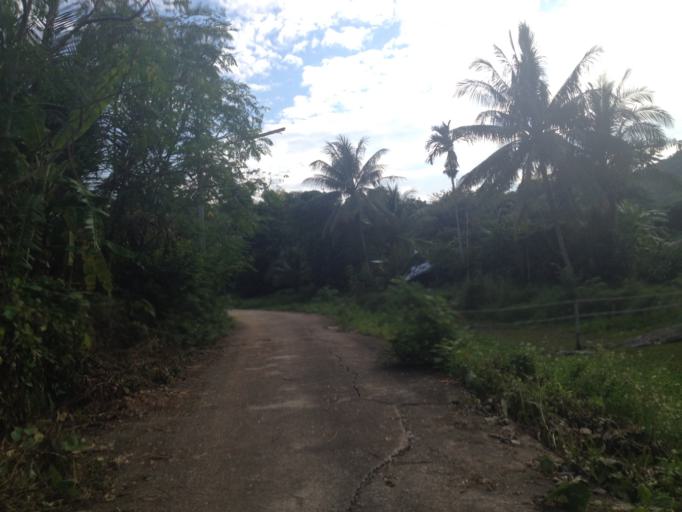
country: TH
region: Chiang Mai
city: Hang Dong
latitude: 18.7323
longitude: 98.9042
